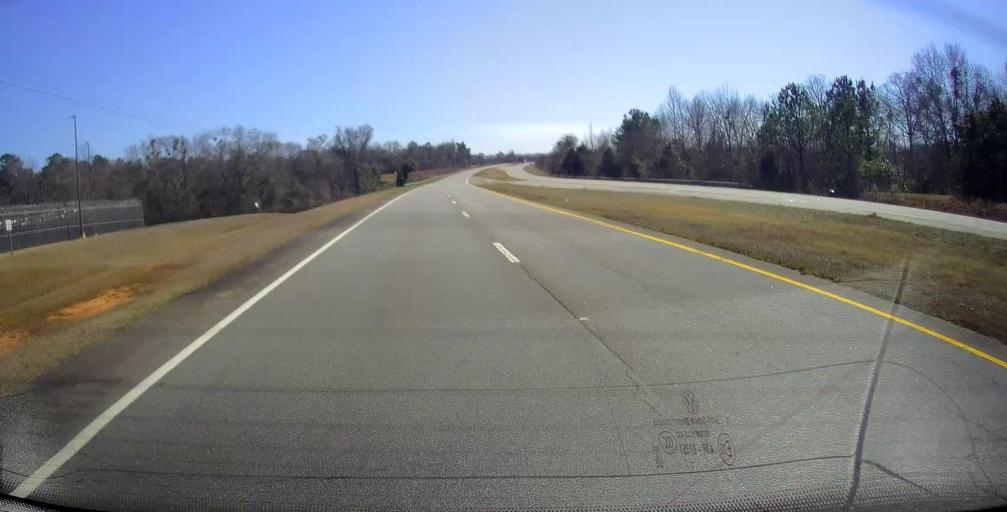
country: US
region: Georgia
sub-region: Houston County
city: Perry
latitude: 32.4640
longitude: -83.6955
